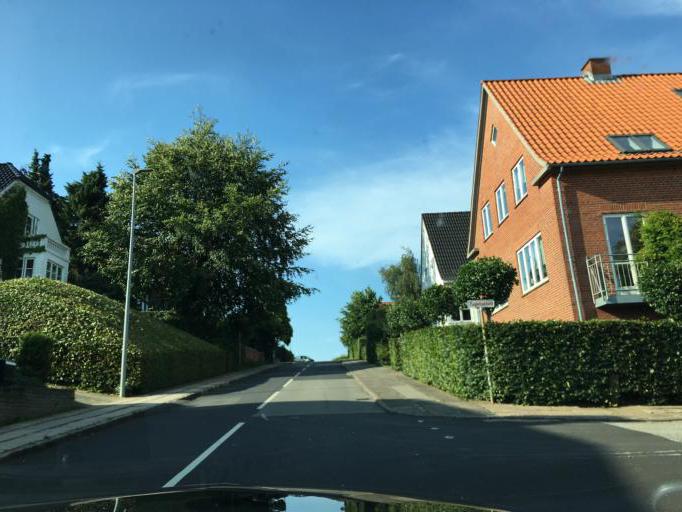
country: DK
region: South Denmark
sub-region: Kolding Kommune
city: Kolding
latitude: 55.4978
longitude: 9.4721
